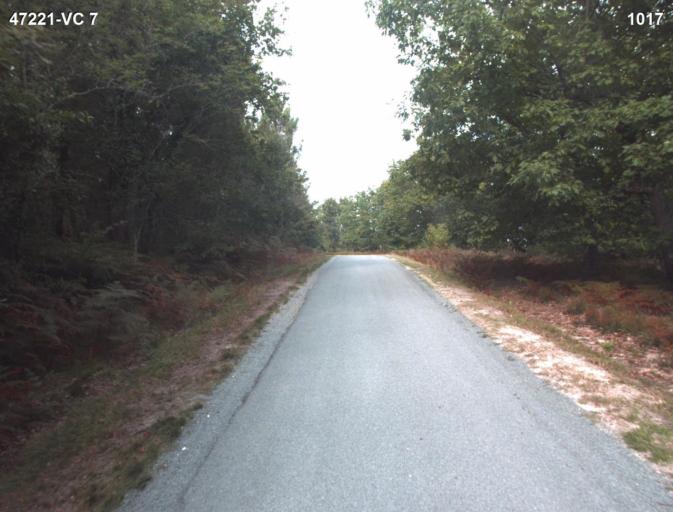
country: FR
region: Aquitaine
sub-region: Departement du Lot-et-Garonne
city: Mezin
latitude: 44.0908
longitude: 0.2237
